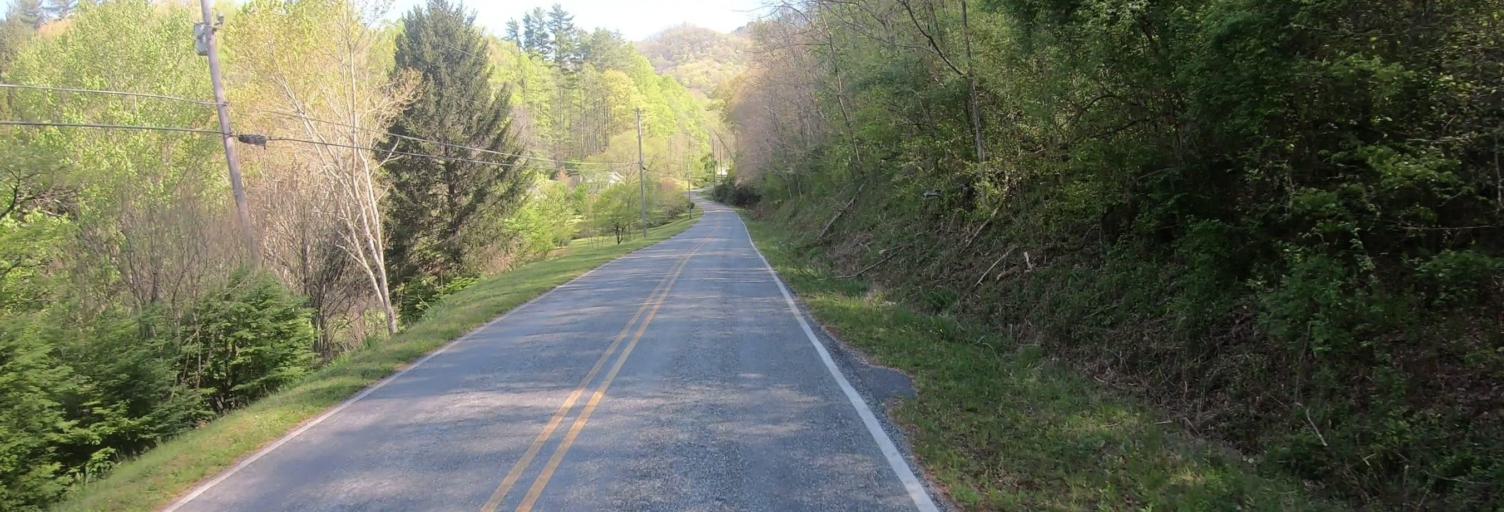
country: US
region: North Carolina
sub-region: Swain County
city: Bryson City
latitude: 35.3787
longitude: -83.4524
